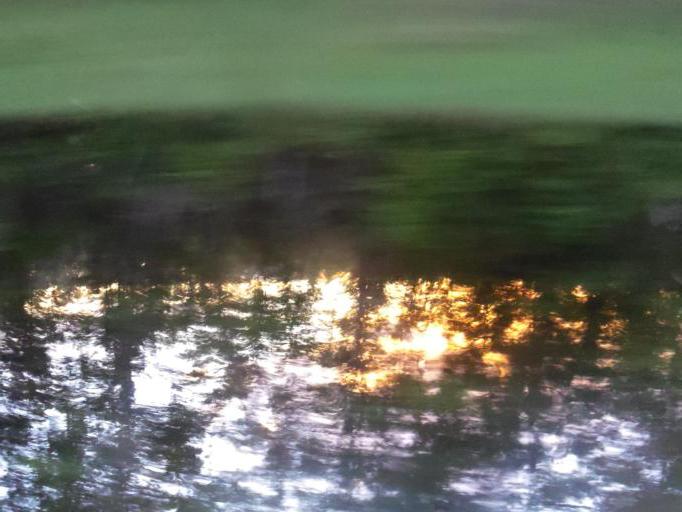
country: US
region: Georgia
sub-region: Camden County
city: Kingsland
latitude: 30.7481
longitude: -81.6878
